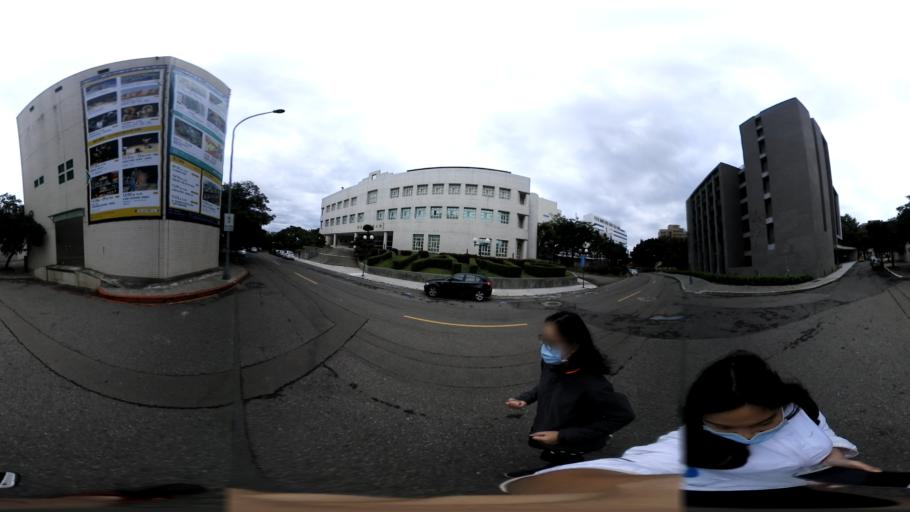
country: TW
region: Taiwan
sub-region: Hsinchu
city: Hsinchu
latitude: 24.7861
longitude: 121.0003
